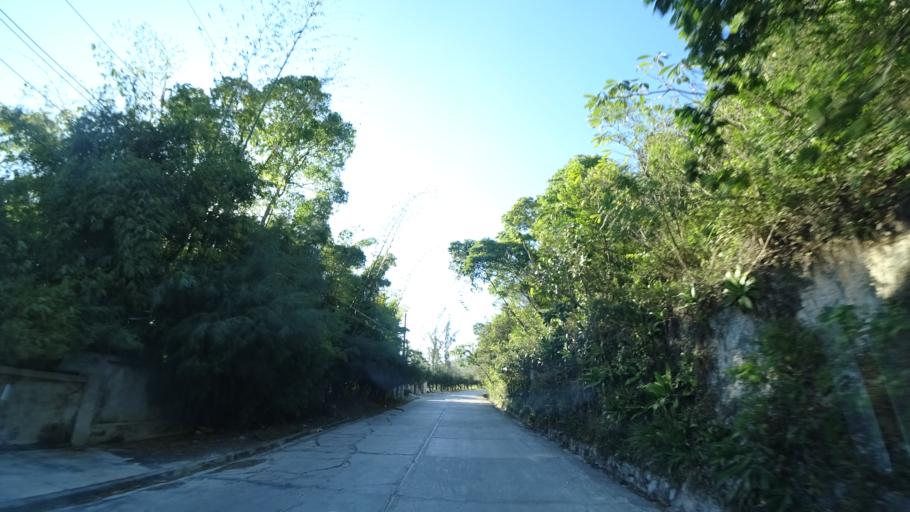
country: HT
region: Ouest
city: Port-au-Prince
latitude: 18.4951
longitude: -72.3420
